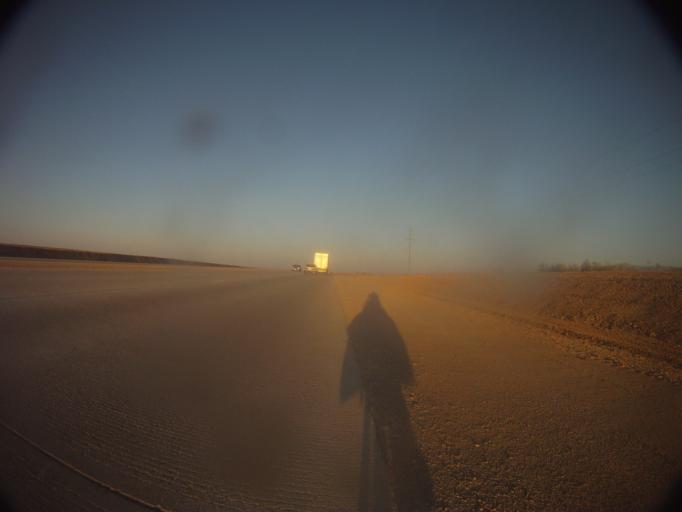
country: KZ
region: Zhambyl
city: Sarykemer
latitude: 43.0047
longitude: 71.6389
